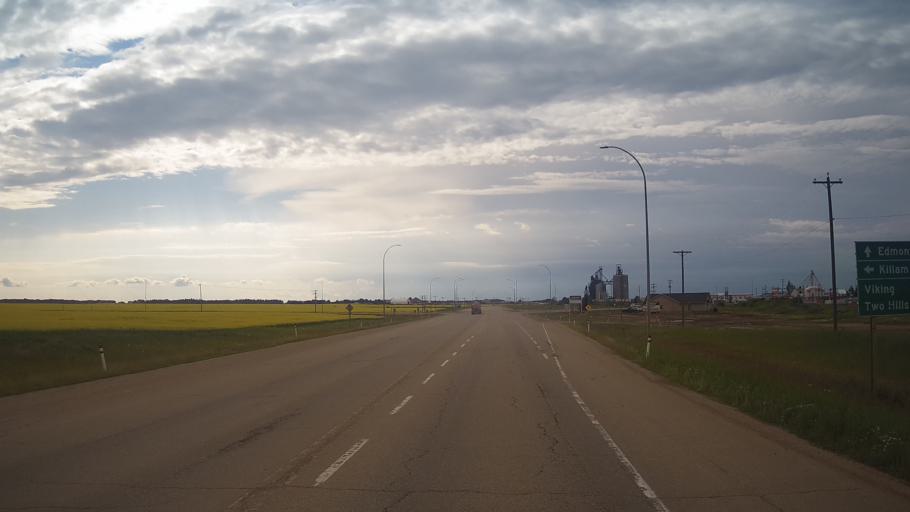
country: CA
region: Alberta
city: Viking
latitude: 53.0918
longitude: -111.7801
